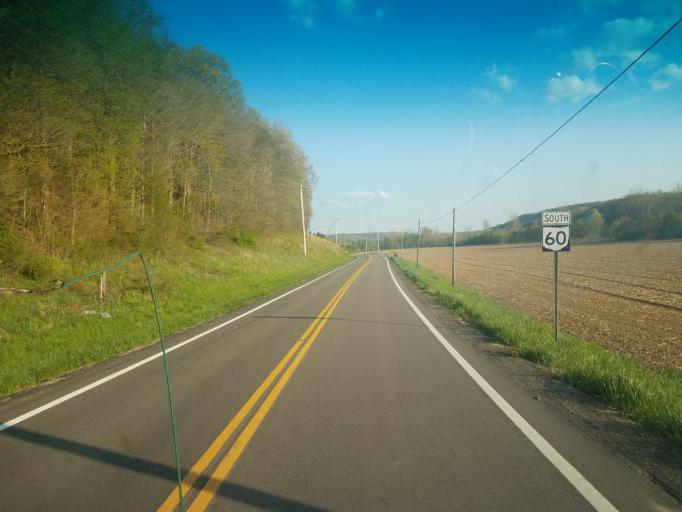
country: US
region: Ohio
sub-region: Holmes County
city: Millersburg
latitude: 40.5175
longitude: -81.9947
